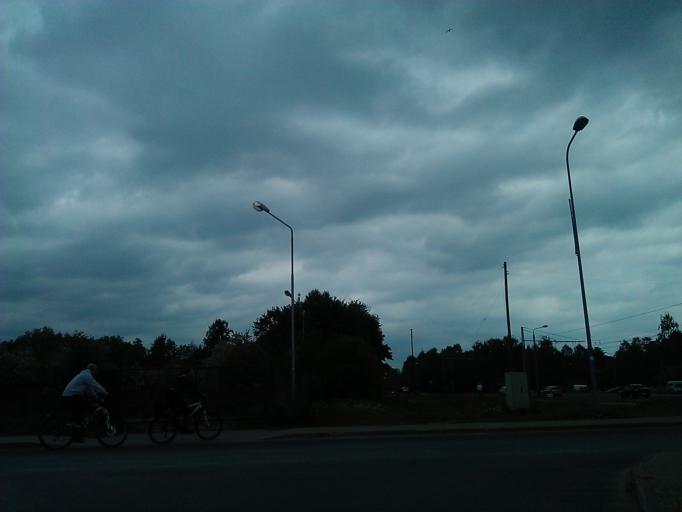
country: LV
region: Kekava
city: Balozi
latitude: 56.9030
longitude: 24.0931
